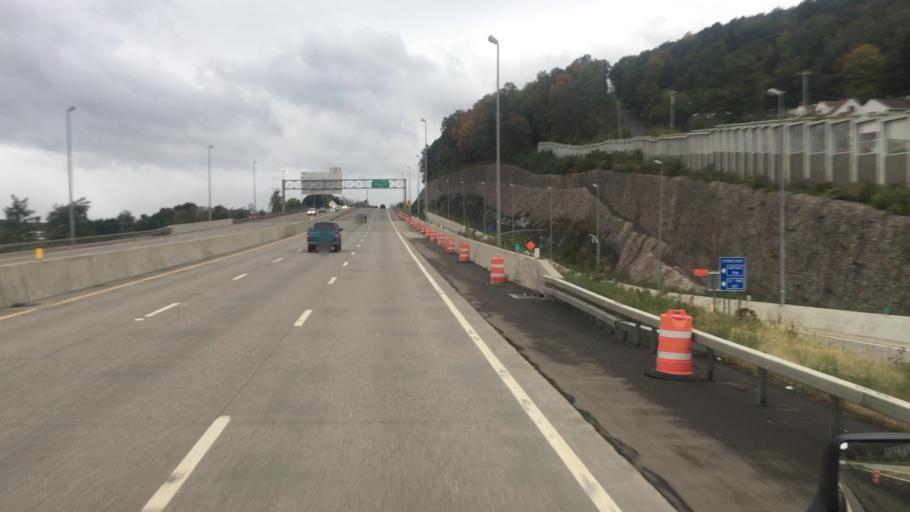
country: US
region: New York
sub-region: Broome County
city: Binghamton
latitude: 42.1136
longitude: -75.9259
